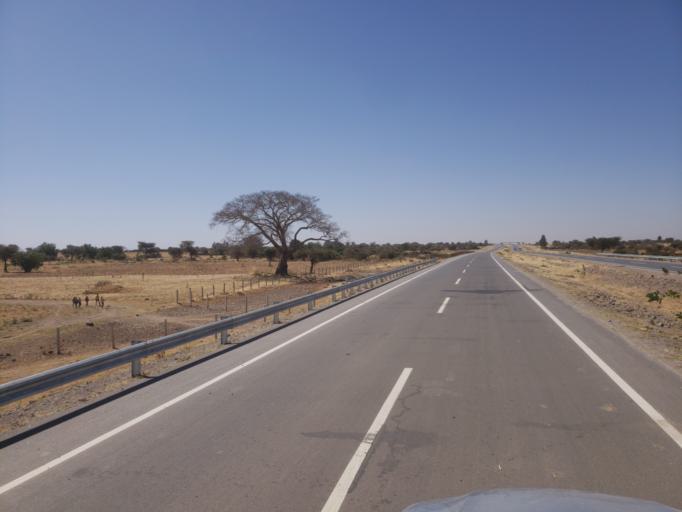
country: ET
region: Oromiya
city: Ziway
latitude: 8.2605
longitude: 38.8997
